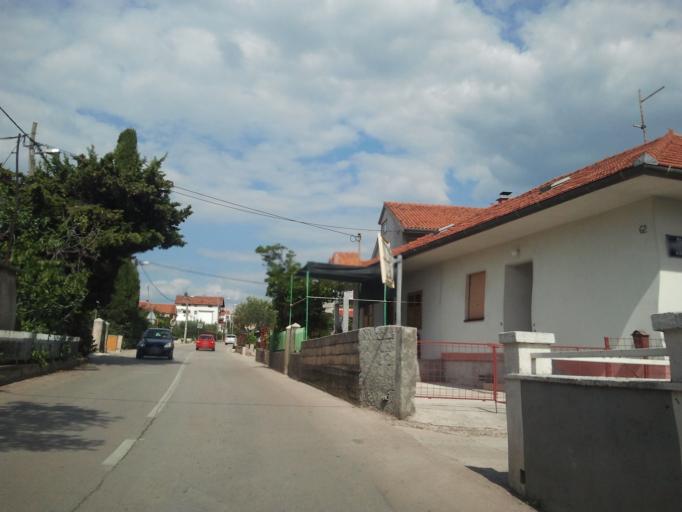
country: HR
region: Zadarska
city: Zadar
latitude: 44.1204
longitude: 15.2490
